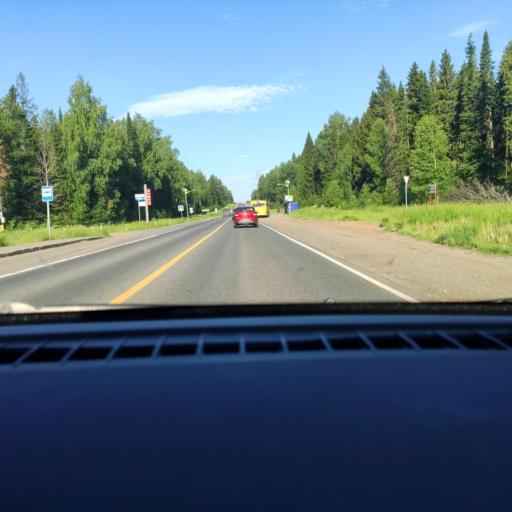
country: RU
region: Udmurtiya
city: Khokhryaki
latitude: 56.9162
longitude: 53.4401
